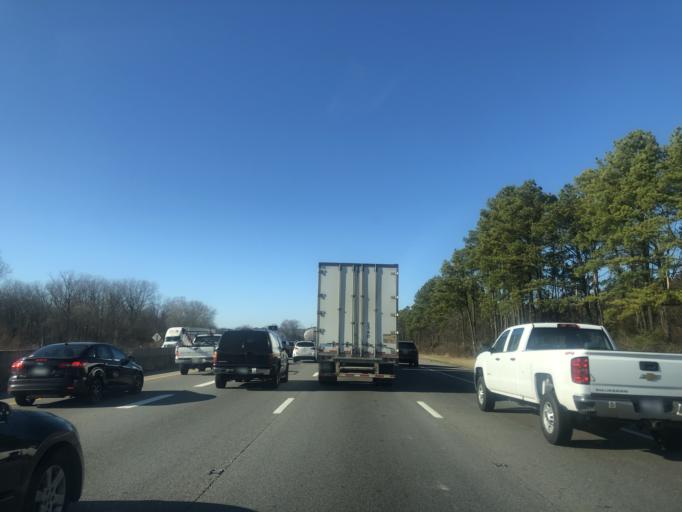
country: US
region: Tennessee
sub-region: Rutherford County
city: La Vergne
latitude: 36.0496
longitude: -86.6657
